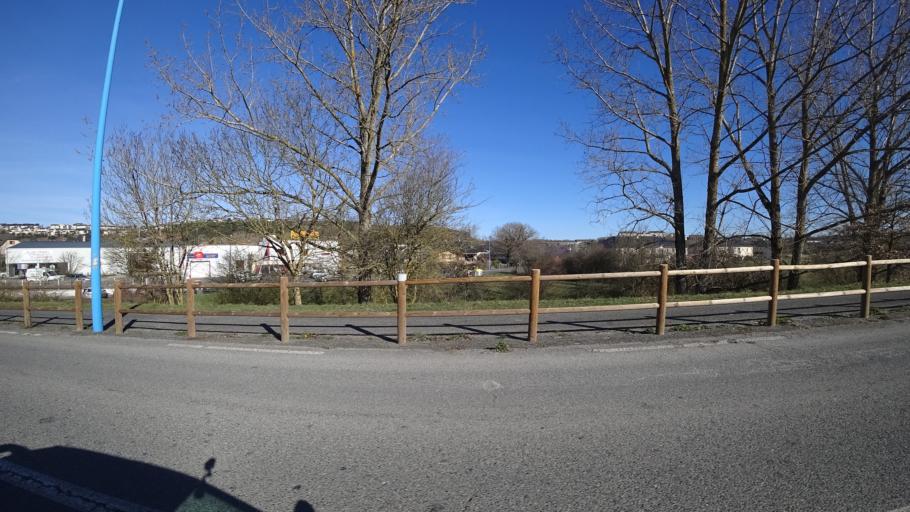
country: FR
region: Midi-Pyrenees
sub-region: Departement de l'Aveyron
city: Rodez
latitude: 44.3727
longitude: 2.5832
